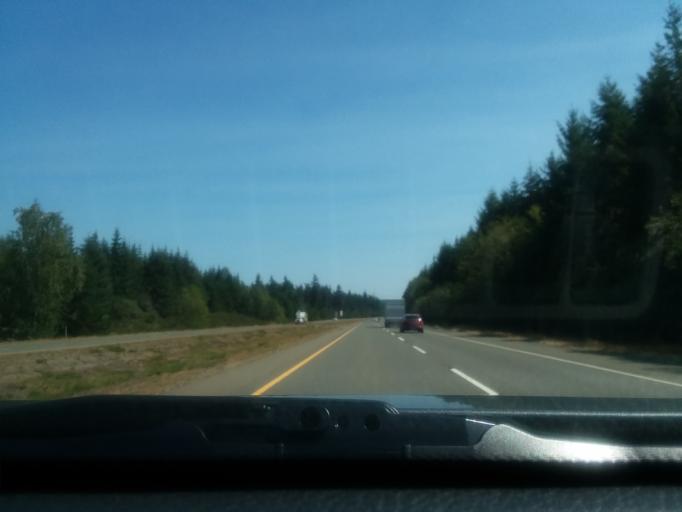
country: CA
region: British Columbia
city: Port Alberni
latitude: 49.3972
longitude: -124.6565
